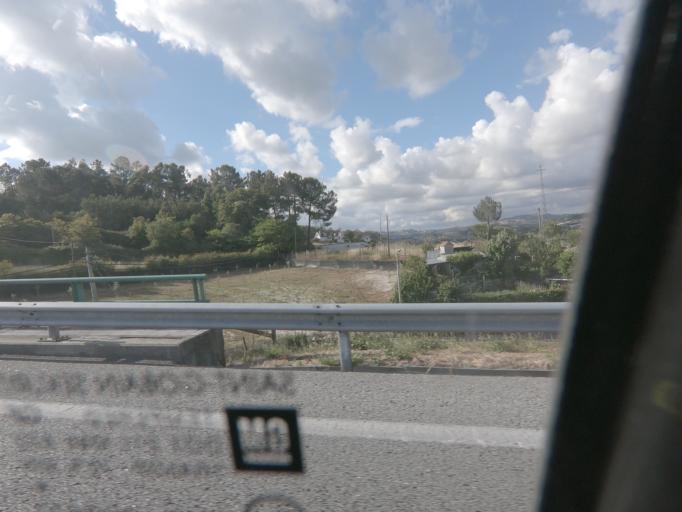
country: PT
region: Porto
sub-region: Marco de Canaveses
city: Marco de Canavezes
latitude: 41.2360
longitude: -8.1853
